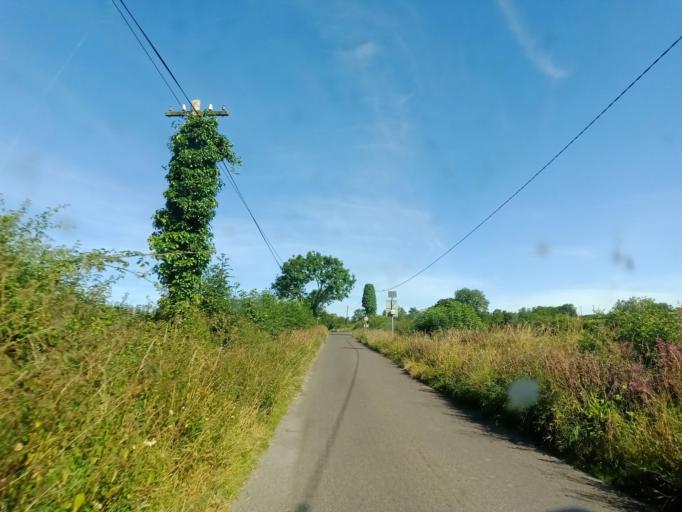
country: IE
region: Leinster
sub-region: Kilkenny
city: Ballyragget
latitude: 52.7586
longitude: -7.4047
